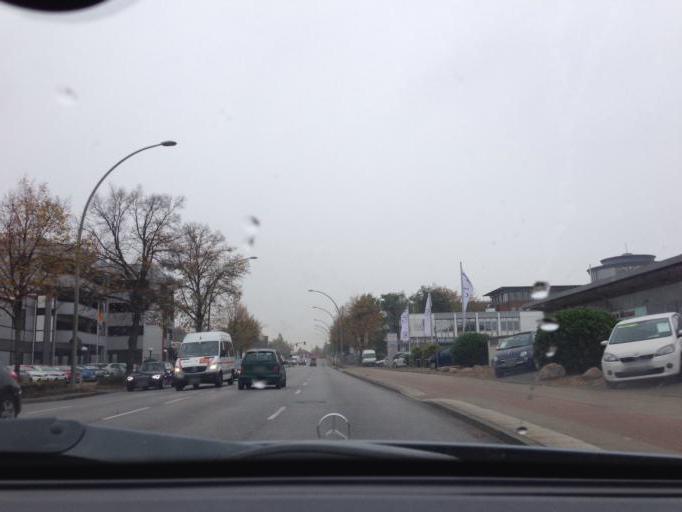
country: DE
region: Hamburg
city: Wandsbek
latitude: 53.5734
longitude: 10.1045
